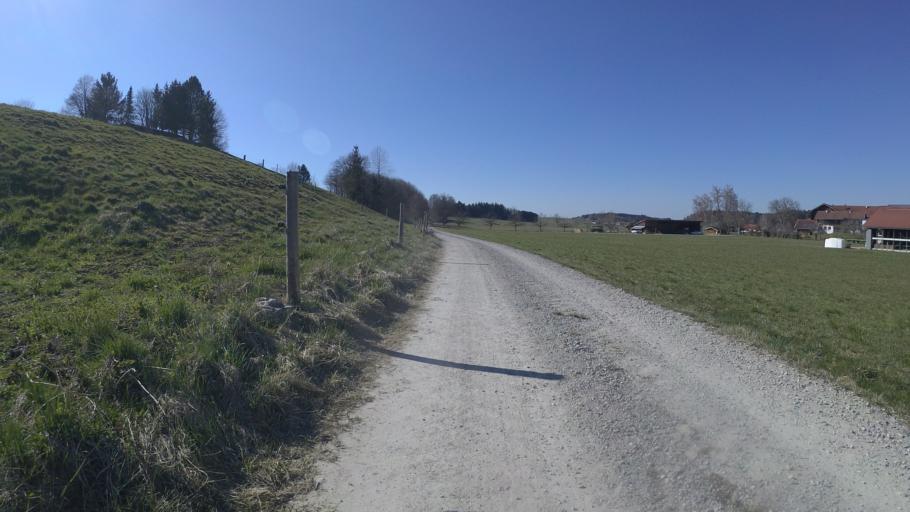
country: DE
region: Bavaria
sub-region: Upper Bavaria
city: Seeon-Seebruck
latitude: 47.9512
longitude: 12.5164
